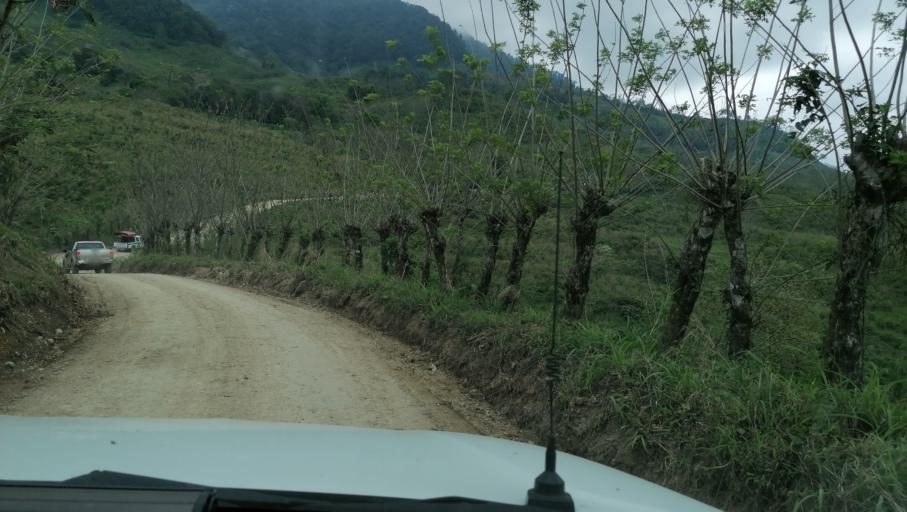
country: MX
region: Chiapas
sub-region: Ocotepec
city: San Pablo Huacano
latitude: 17.2686
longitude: -93.2612
